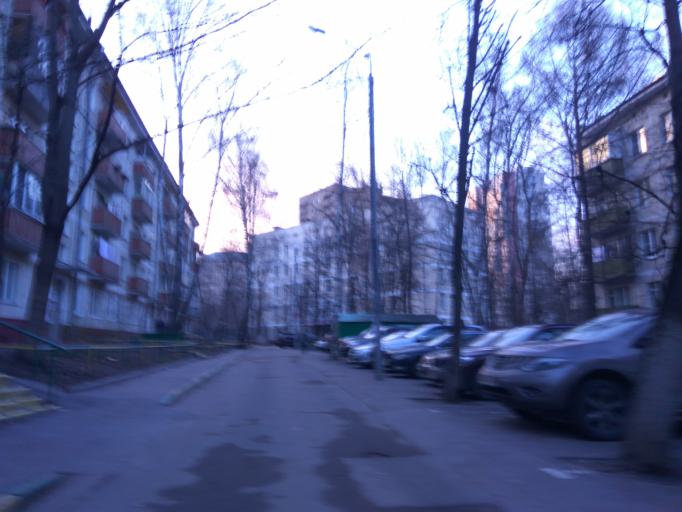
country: RU
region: Moskovskaya
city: Semenovskoye
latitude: 55.6794
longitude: 37.5403
